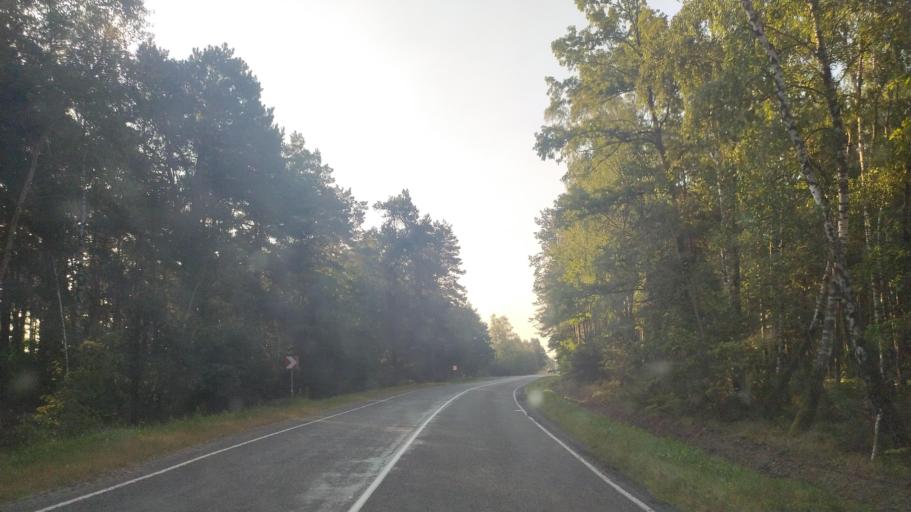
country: BY
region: Brest
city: Drahichyn
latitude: 52.3065
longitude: 25.0467
